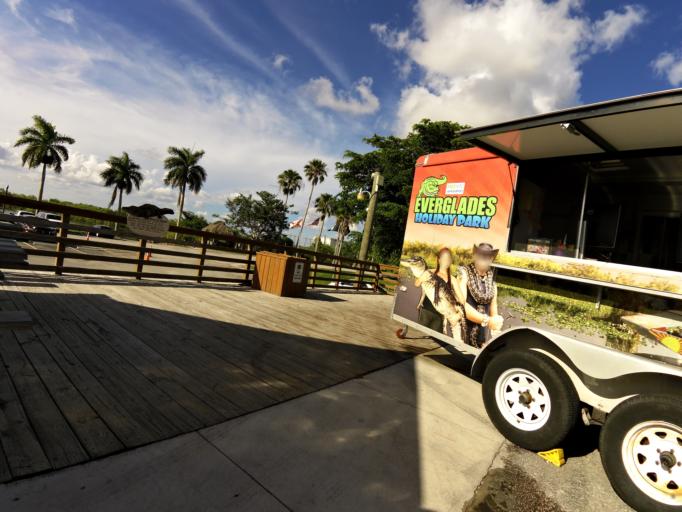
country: US
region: Florida
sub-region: Broward County
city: Weston
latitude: 26.0606
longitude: -80.4445
